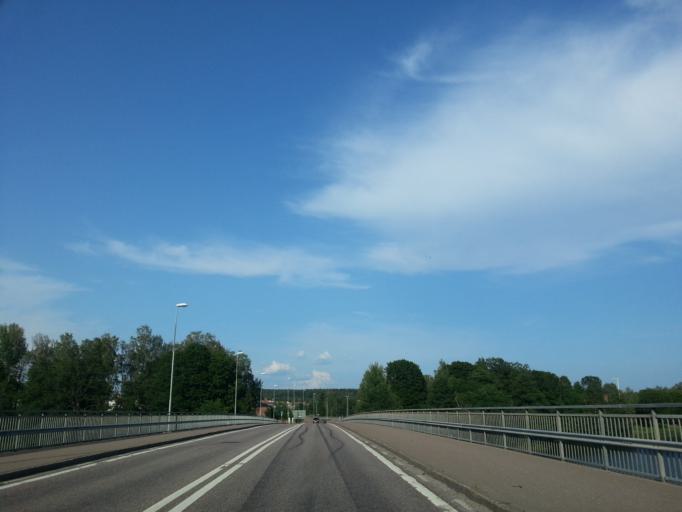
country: SE
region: Vaestmanland
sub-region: Fagersta Kommun
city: Fagersta
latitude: 59.9842
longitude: 15.8096
